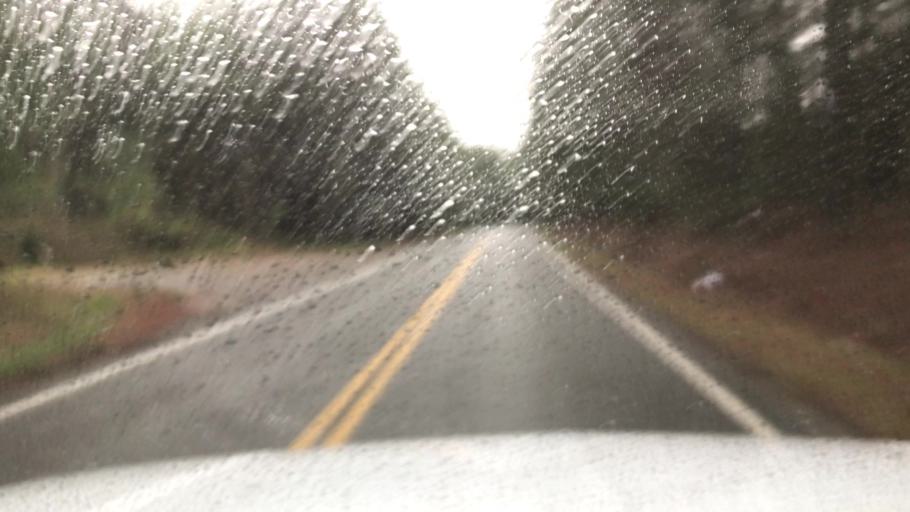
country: US
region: Virginia
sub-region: Henrico County
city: Short Pump
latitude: 37.6359
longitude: -77.6791
